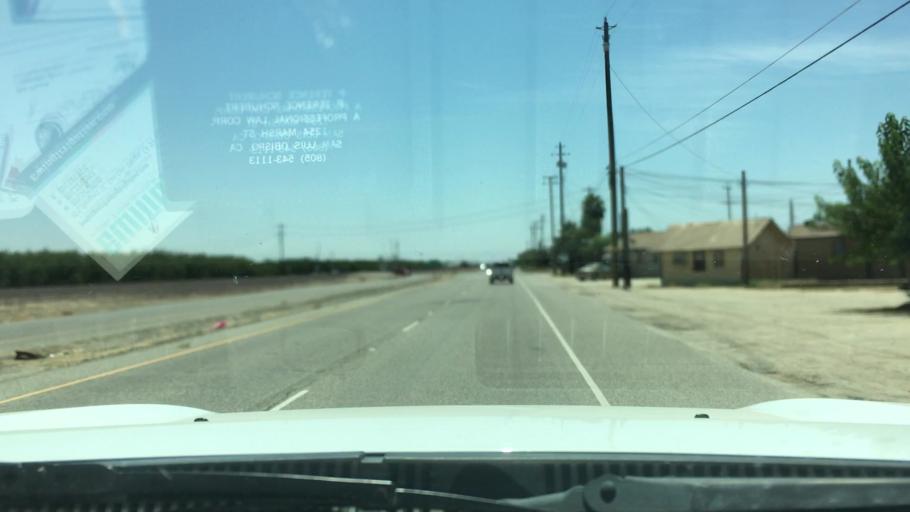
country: US
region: California
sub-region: Kern County
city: Shafter
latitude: 35.5156
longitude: -119.2899
